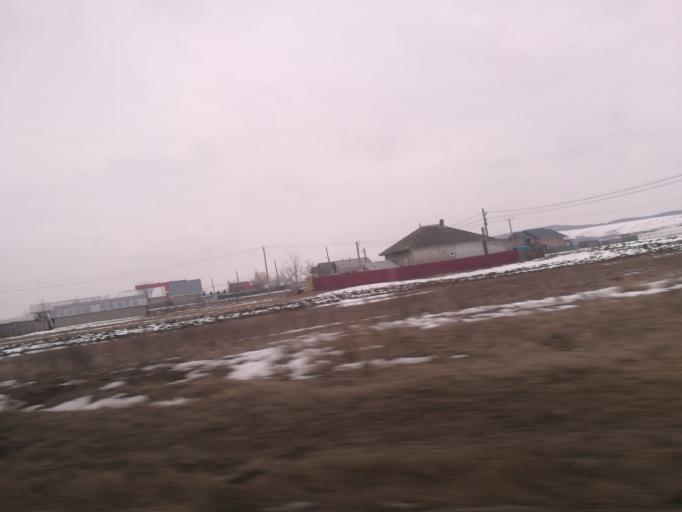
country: RO
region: Iasi
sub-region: Comuna Valea Seaca
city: Topile
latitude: 47.2404
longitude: 26.6701
